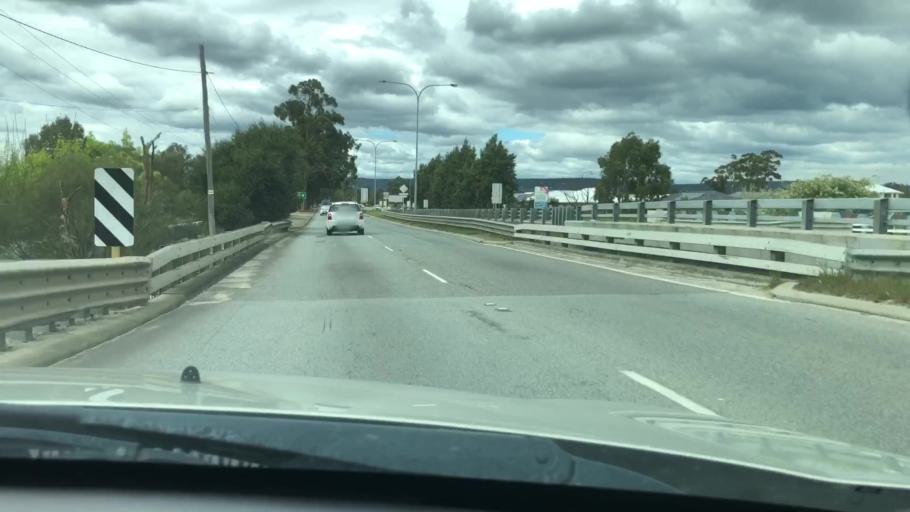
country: AU
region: Western Australia
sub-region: Armadale
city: Seville Grove
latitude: -32.1471
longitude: 115.9739
